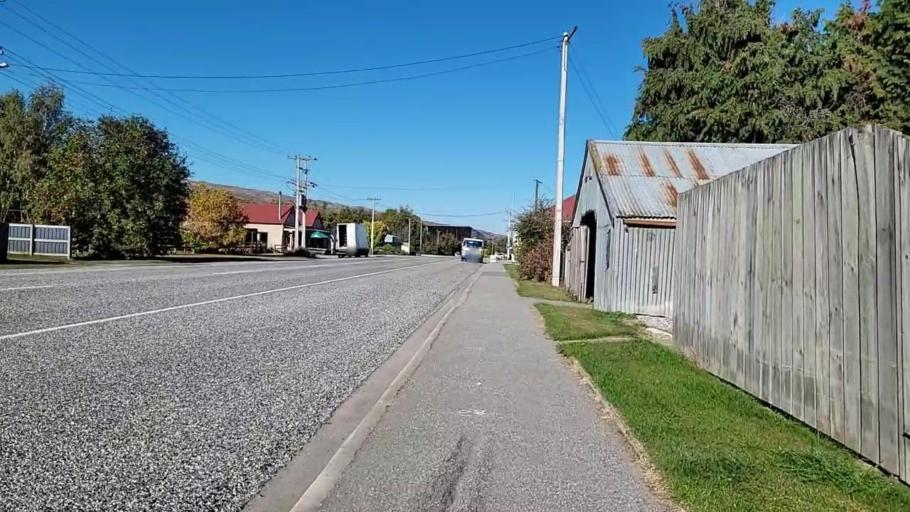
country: NZ
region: Otago
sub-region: Queenstown-Lakes District
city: Wanaka
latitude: -45.0063
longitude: 169.9135
